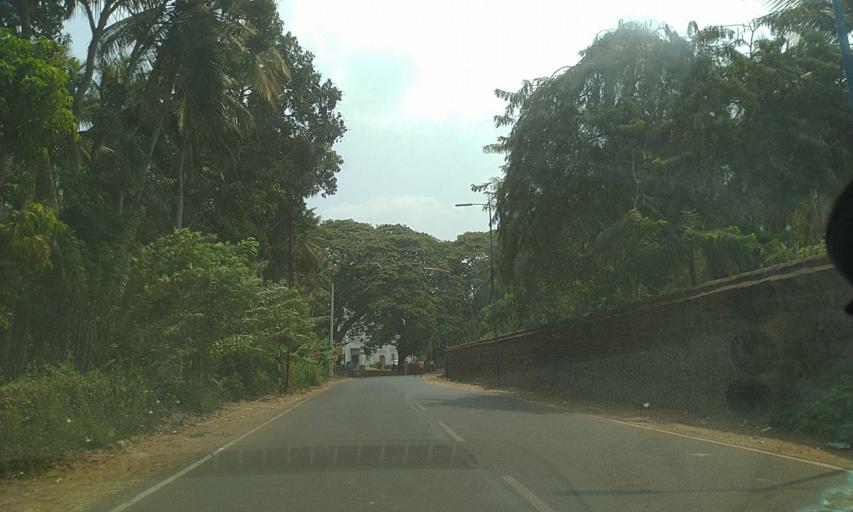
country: IN
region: Goa
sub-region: North Goa
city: Jua
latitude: 15.5050
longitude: 73.9131
